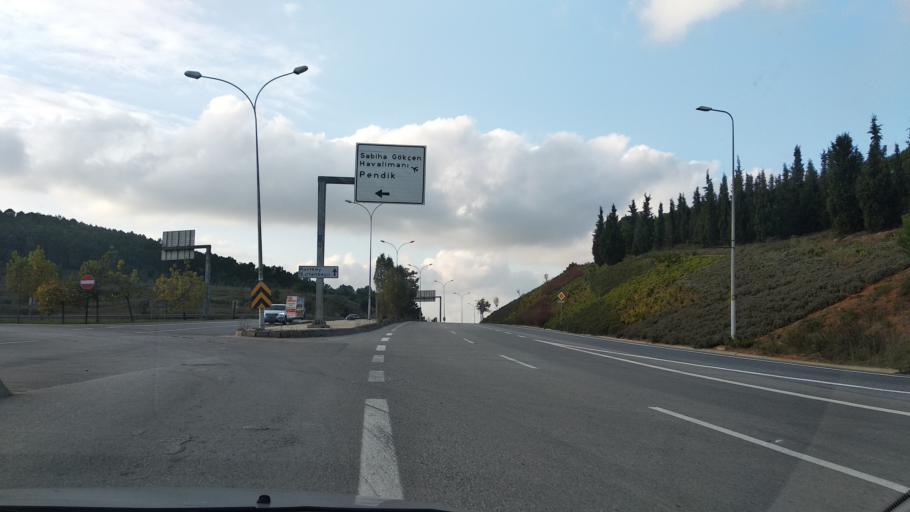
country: TR
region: Istanbul
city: Sultanbeyli
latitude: 40.9232
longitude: 29.3397
